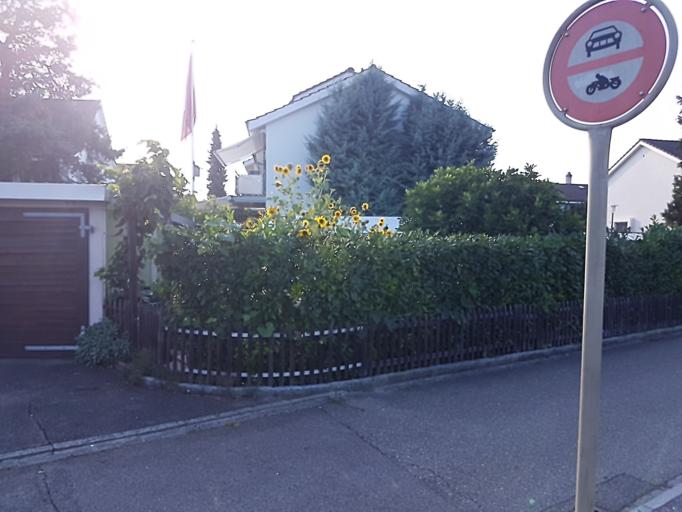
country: CH
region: Basel-Landschaft
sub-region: Bezirk Arlesheim
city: Aesch
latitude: 47.4885
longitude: 7.5903
